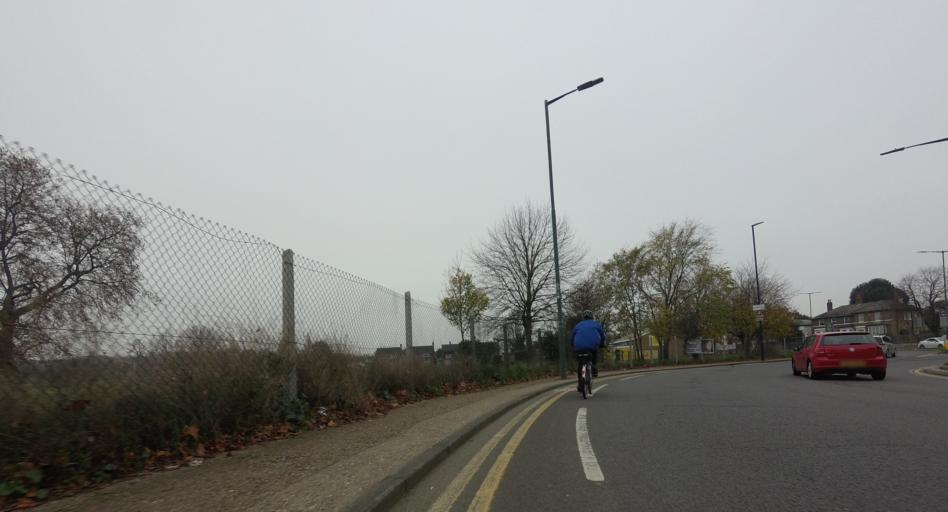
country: GB
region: England
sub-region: Greater London
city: Bexley
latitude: 51.4452
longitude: 0.1537
